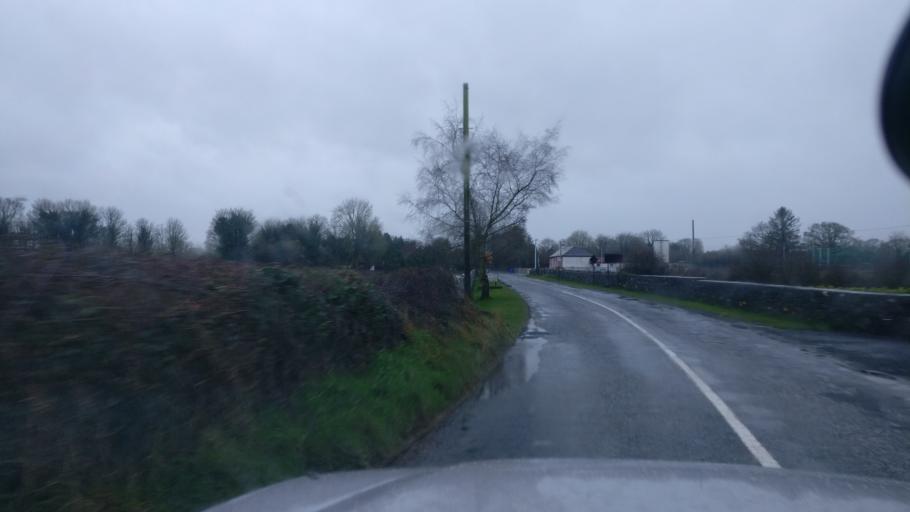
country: IE
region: Connaught
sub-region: County Galway
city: Ballinasloe
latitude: 53.2406
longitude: -8.1715
